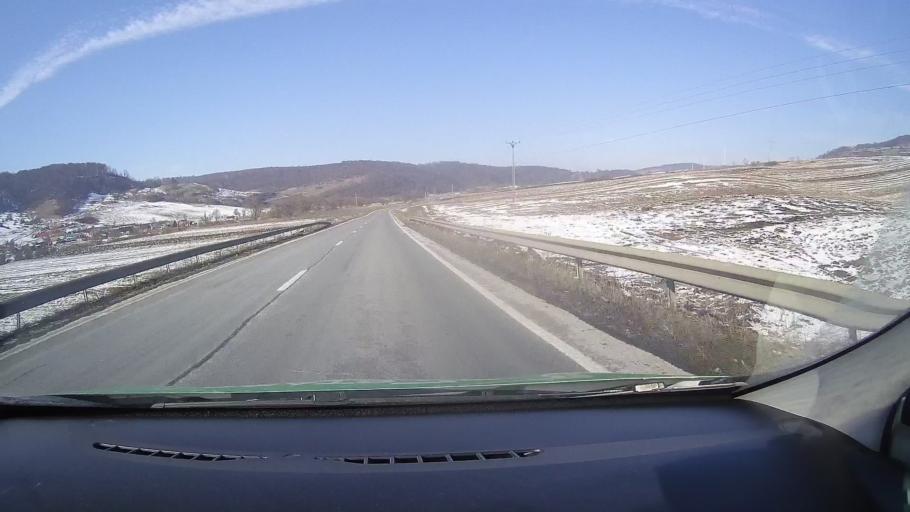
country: RO
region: Brasov
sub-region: Comuna Bunesti
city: Bunesti
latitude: 46.1267
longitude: 25.0206
